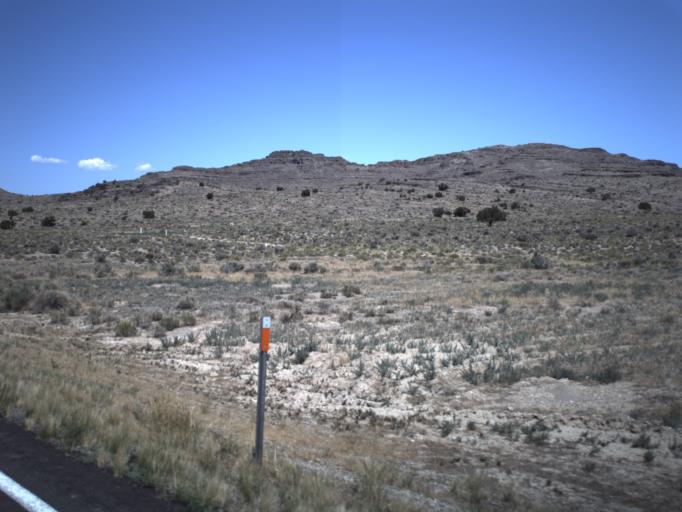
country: US
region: Utah
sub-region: Beaver County
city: Milford
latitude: 39.0780
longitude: -113.6927
